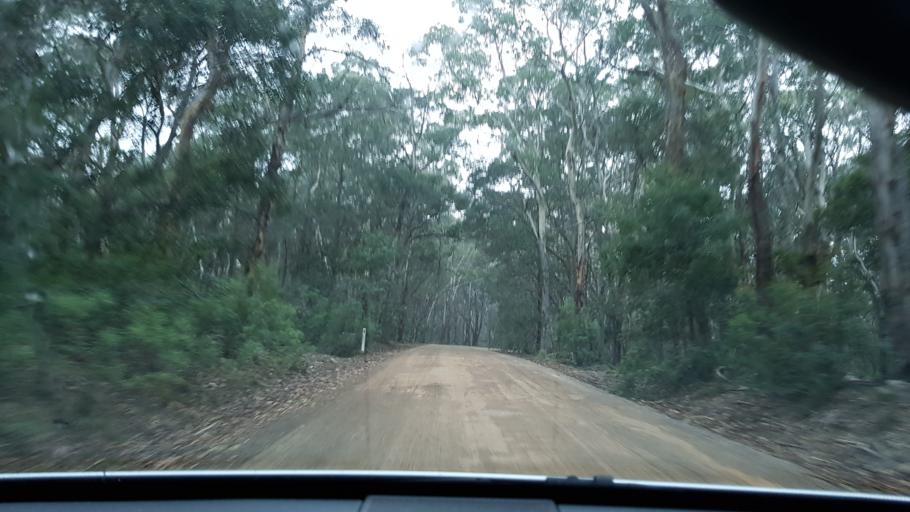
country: AU
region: New South Wales
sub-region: Oberon
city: Oberon
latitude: -33.9795
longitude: 150.0565
